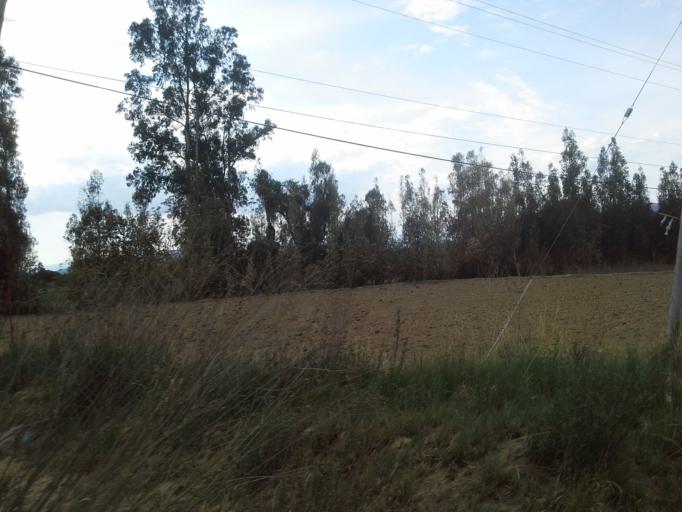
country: BO
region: Cochabamba
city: Tarata
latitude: -17.5741
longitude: -66.0142
